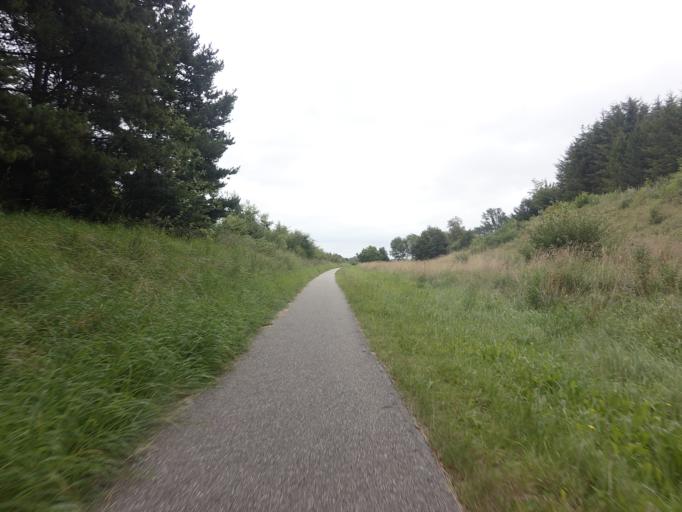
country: DK
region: Central Jutland
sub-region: Horsens Kommune
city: Braedstrup
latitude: 56.0253
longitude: 9.5483
